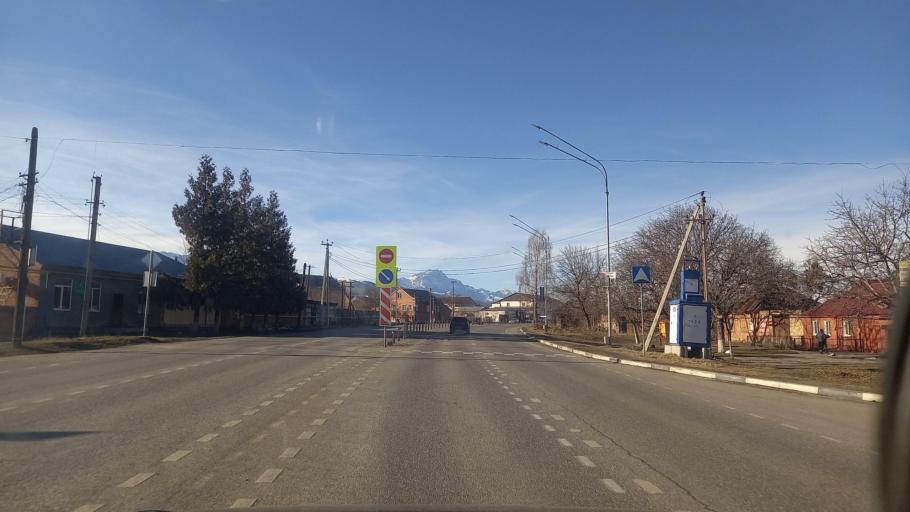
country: RU
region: North Ossetia
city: Gizel'
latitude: 43.0256
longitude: 44.5724
